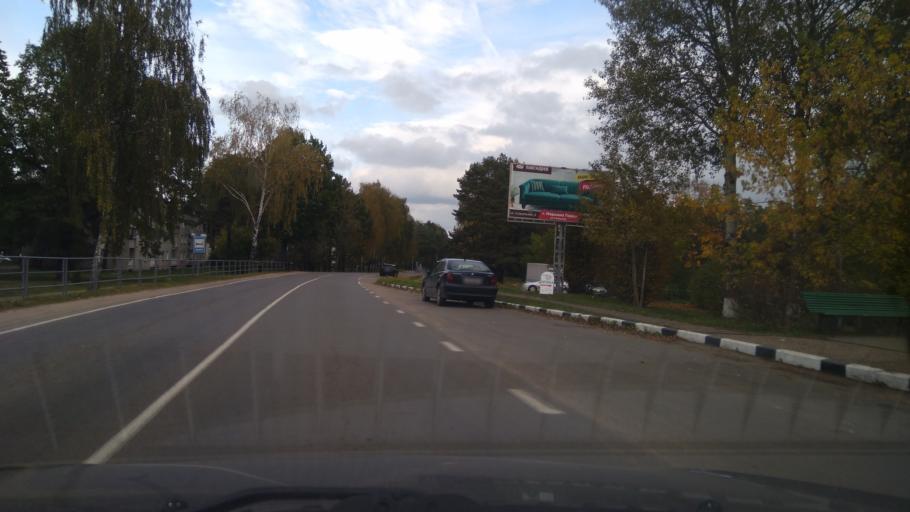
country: BY
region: Minsk
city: Svislach
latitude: 53.6460
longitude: 27.9166
